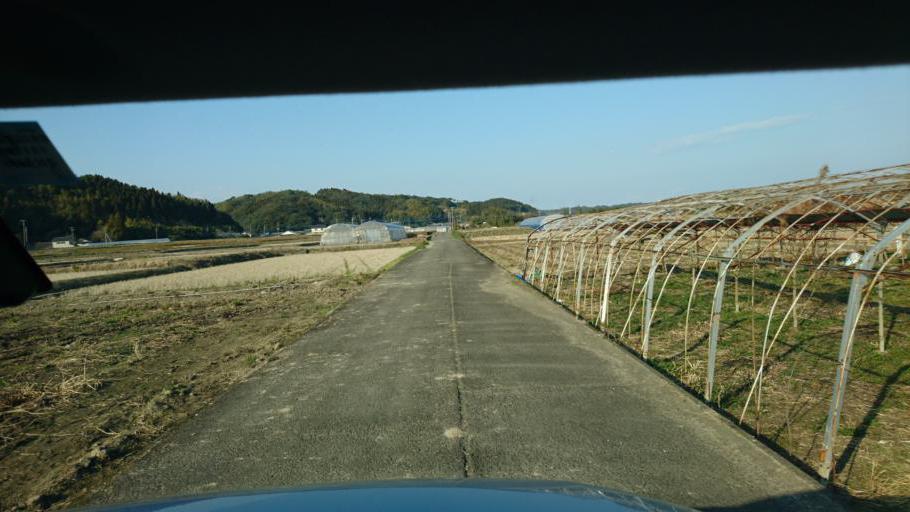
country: JP
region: Miyazaki
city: Miyazaki-shi
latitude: 32.0045
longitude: 131.4362
